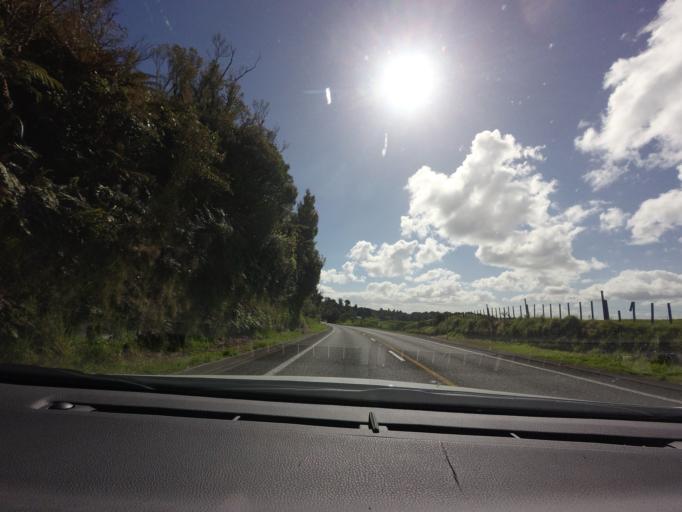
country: NZ
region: Waikato
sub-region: South Waikato District
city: Tokoroa
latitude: -38.0315
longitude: 175.9933
